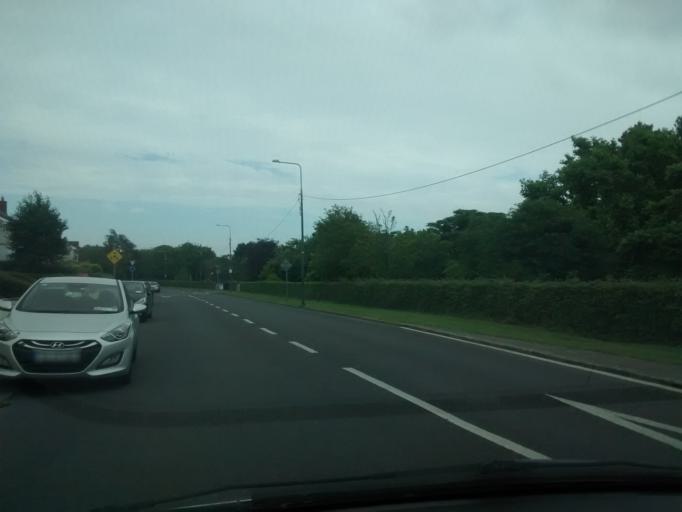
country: IE
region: Leinster
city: Dollymount
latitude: 53.3752
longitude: -6.1846
